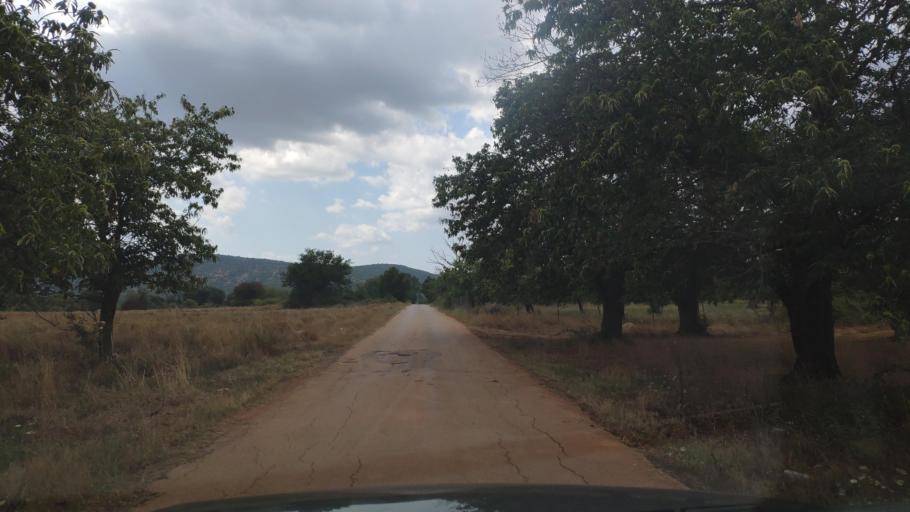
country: GR
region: Peloponnese
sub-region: Nomos Lakonias
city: Kariai
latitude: 37.3162
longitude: 22.4416
